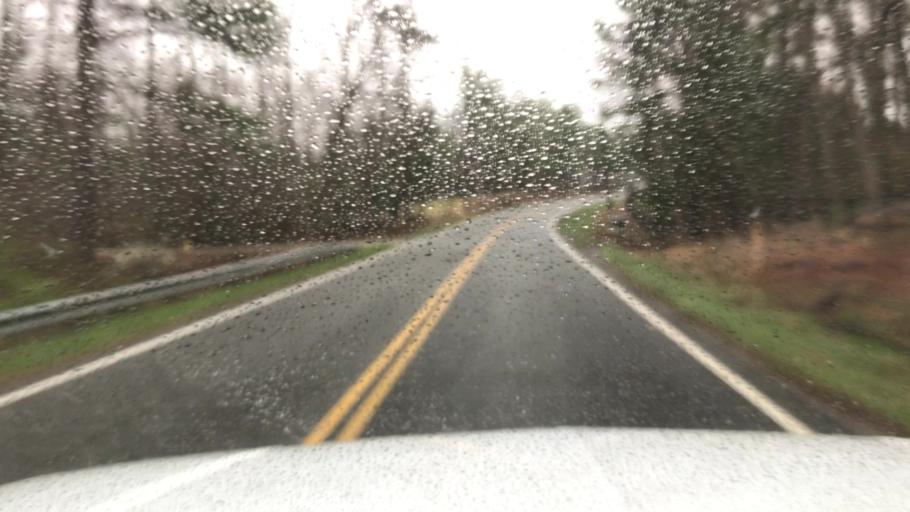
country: US
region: Virginia
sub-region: Henrico County
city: Short Pump
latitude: 37.6524
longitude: -77.6776
